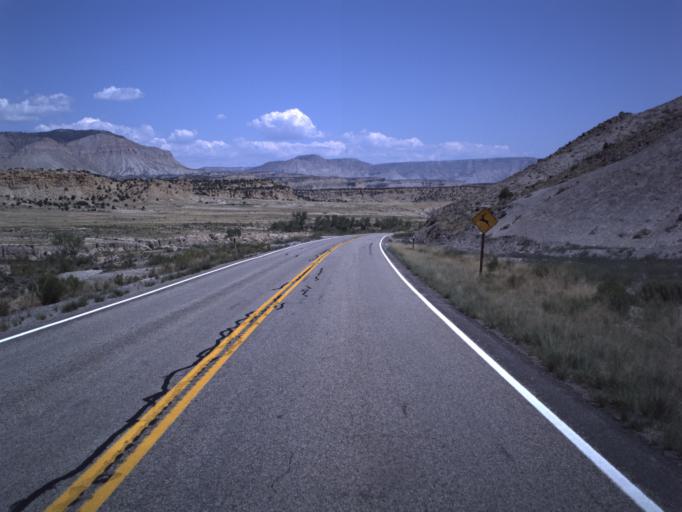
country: US
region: Utah
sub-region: Emery County
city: Ferron
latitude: 38.7842
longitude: -111.3506
